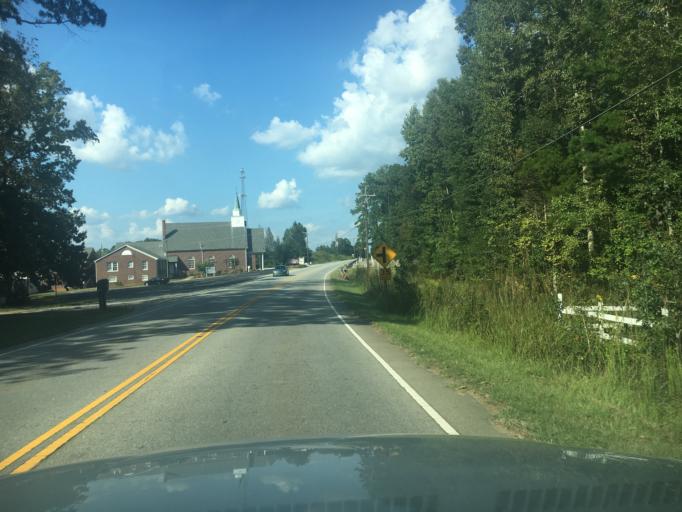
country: US
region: South Carolina
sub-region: Greenville County
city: Simpsonville
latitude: 34.6773
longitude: -82.2574
